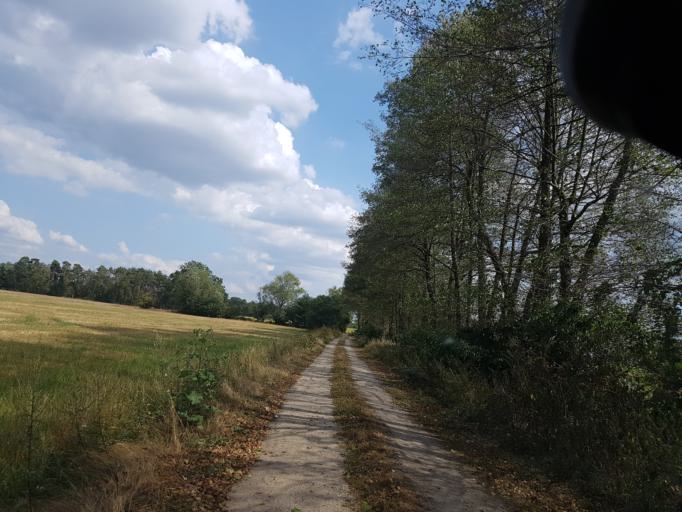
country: DE
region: Brandenburg
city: Calau
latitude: 51.7712
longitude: 13.9667
